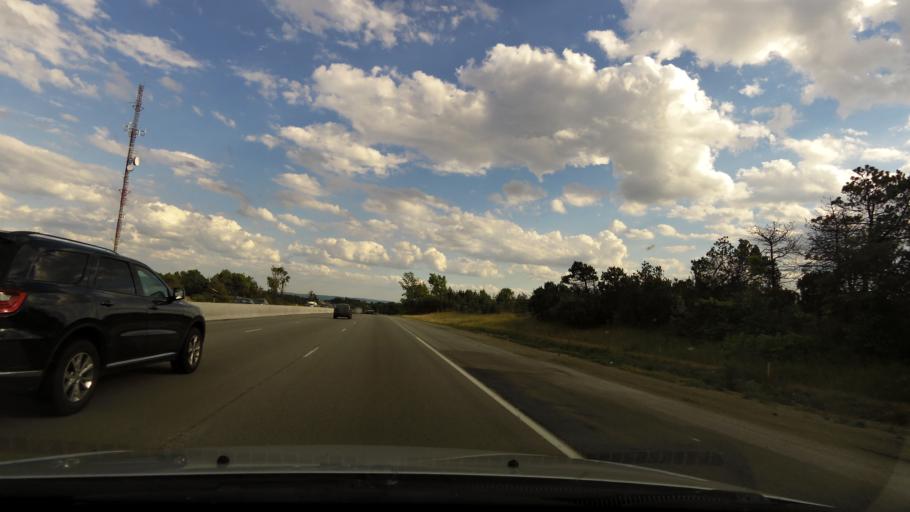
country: CA
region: Ontario
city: Bradford West Gwillimbury
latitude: 44.1475
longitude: -79.6424
